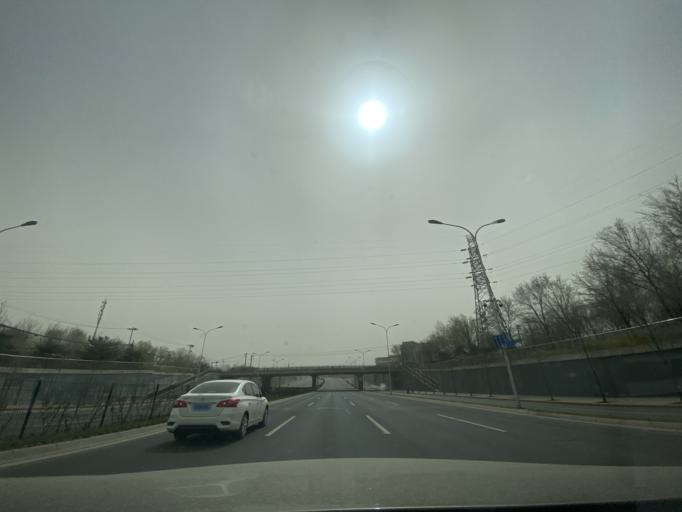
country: CN
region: Beijing
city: Sijiqing
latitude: 39.9502
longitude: 116.2344
